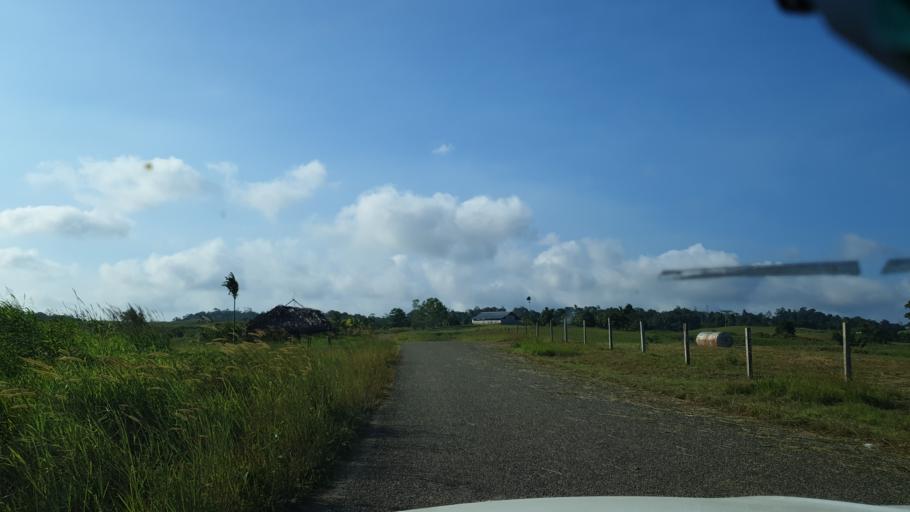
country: PG
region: East Sepik
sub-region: Wewak
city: Wewak
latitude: -3.7049
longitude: 143.7213
